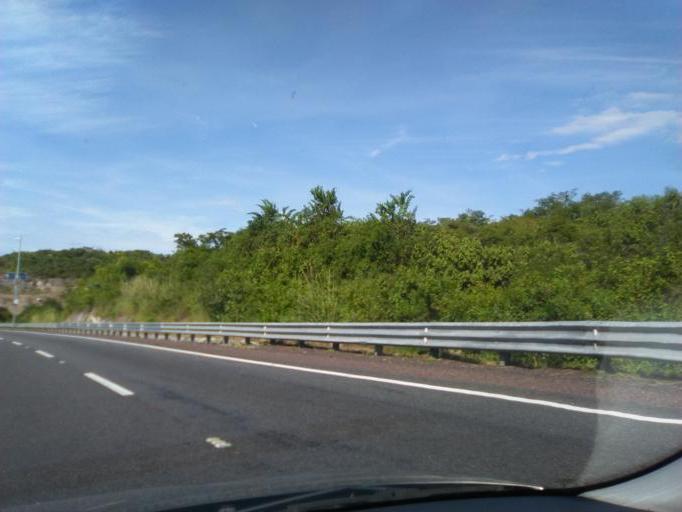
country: MX
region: Guerrero
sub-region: Huitzuco de los Figueroa
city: Ciudad de Huitzuco
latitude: 18.3043
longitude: -99.2006
